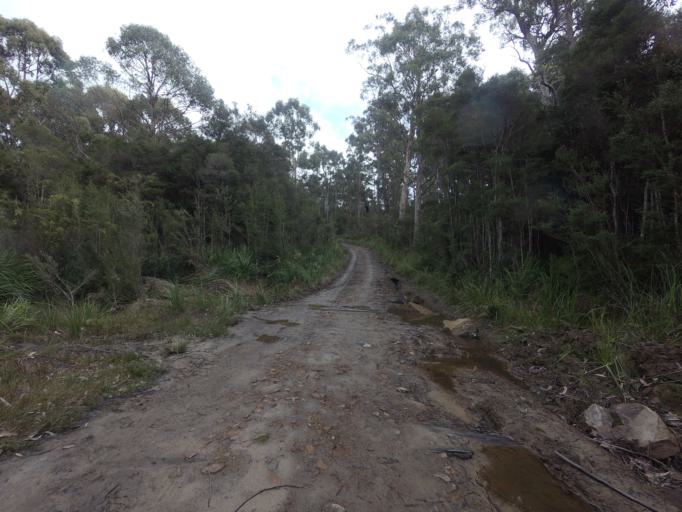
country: AU
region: Tasmania
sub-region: Huon Valley
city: Geeveston
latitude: -43.4725
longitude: 146.9330
